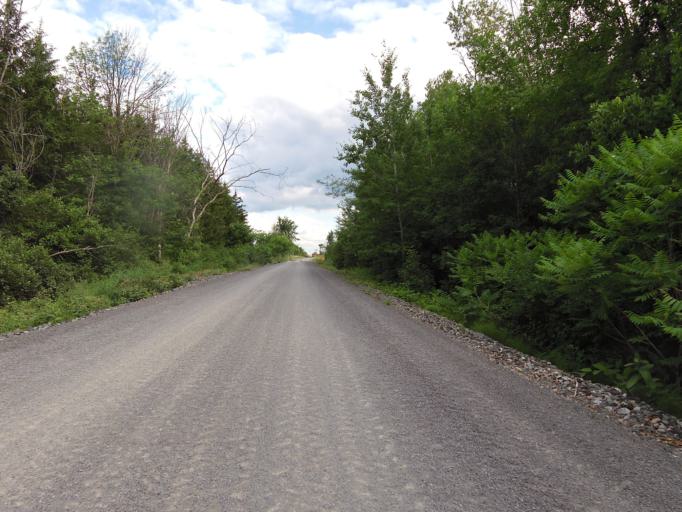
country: CA
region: Ontario
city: Carleton Place
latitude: 45.2821
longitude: -76.2458
